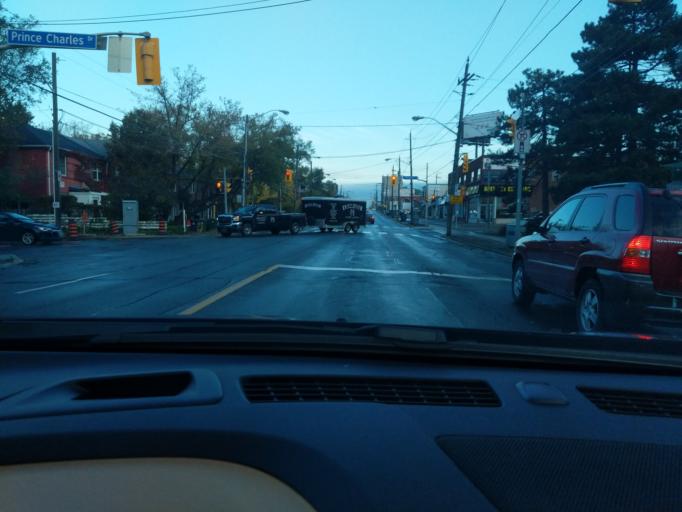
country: CA
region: Ontario
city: Toronto
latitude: 43.7246
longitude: -79.4311
